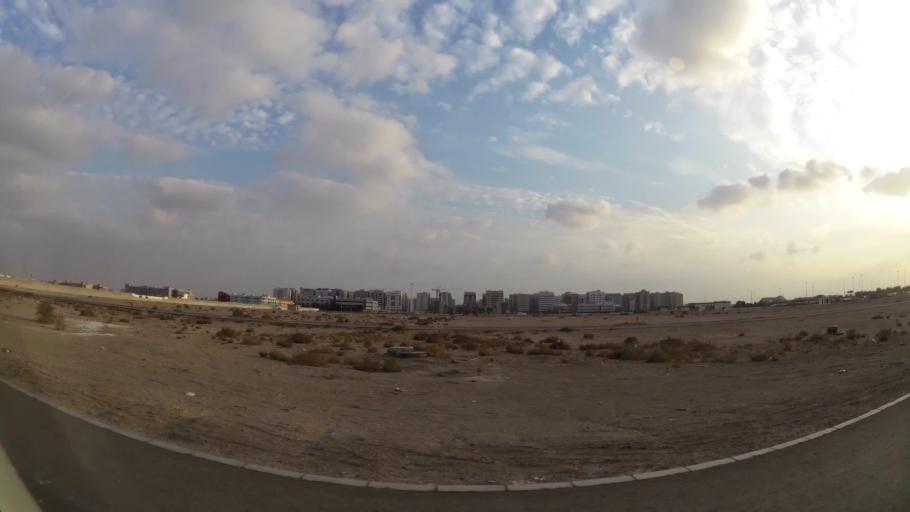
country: AE
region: Abu Dhabi
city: Abu Dhabi
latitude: 24.3515
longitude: 54.5339
